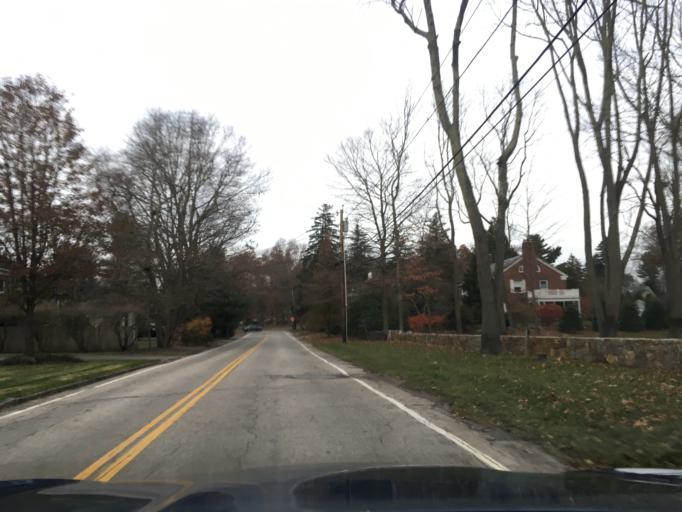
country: US
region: Rhode Island
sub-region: Kent County
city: East Greenwich
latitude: 41.6624
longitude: -71.4591
